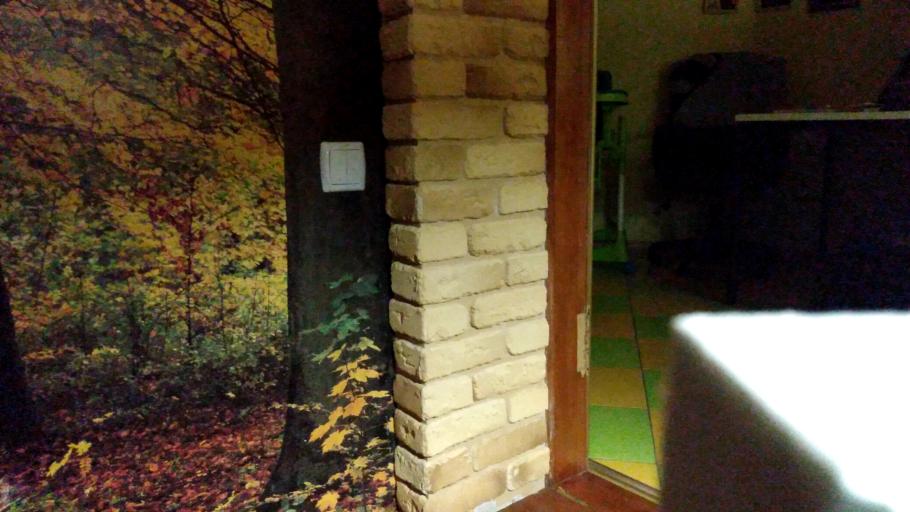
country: RU
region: Vologda
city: Lipin Bor
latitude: 60.8044
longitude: 38.0315
